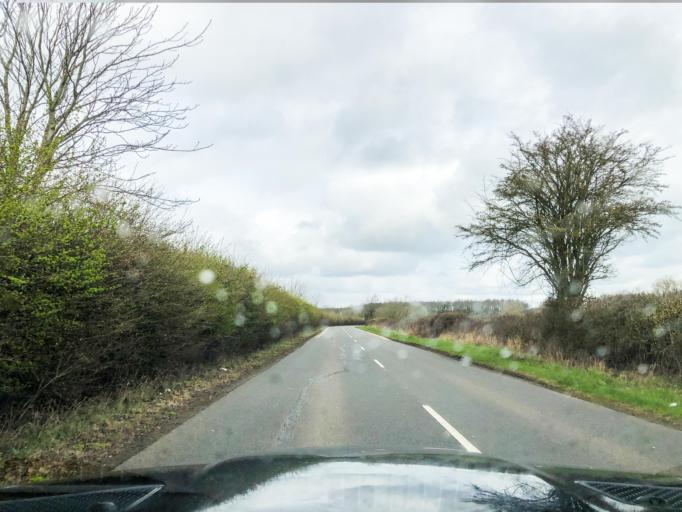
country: GB
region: England
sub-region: Warwickshire
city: Harbury
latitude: 52.1539
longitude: -1.4388
